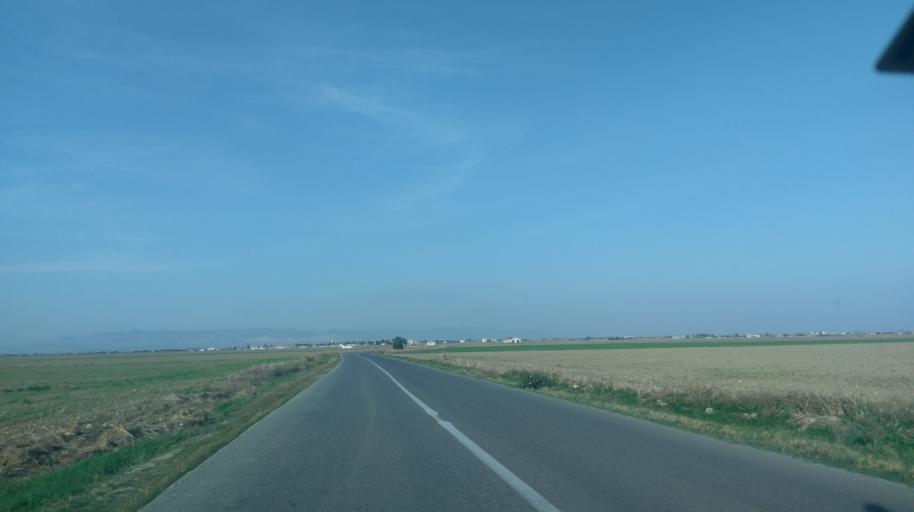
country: CY
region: Ammochostos
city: Achna
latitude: 35.1498
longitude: 33.7491
